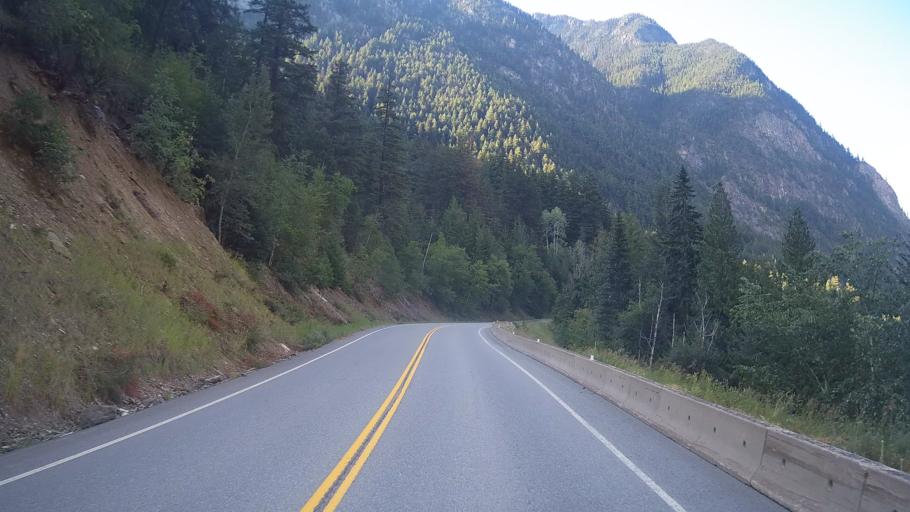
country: CA
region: British Columbia
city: Lillooet
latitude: 50.6359
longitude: -122.0889
